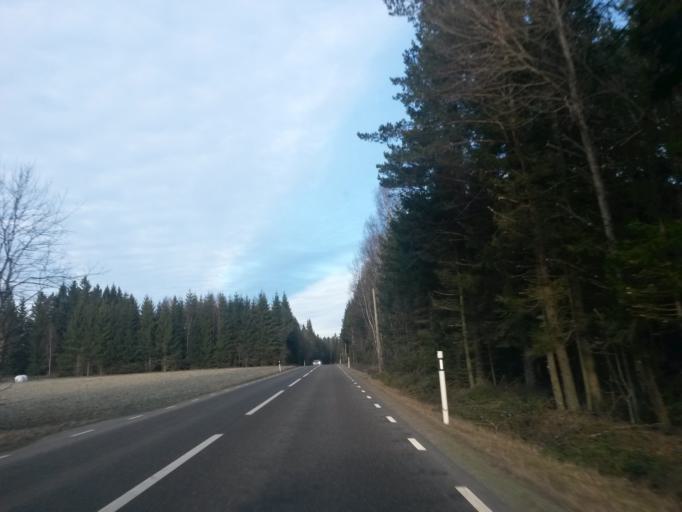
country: SE
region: Vaestra Goetaland
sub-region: Boras Kommun
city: Boras
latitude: 57.8784
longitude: 12.9290
